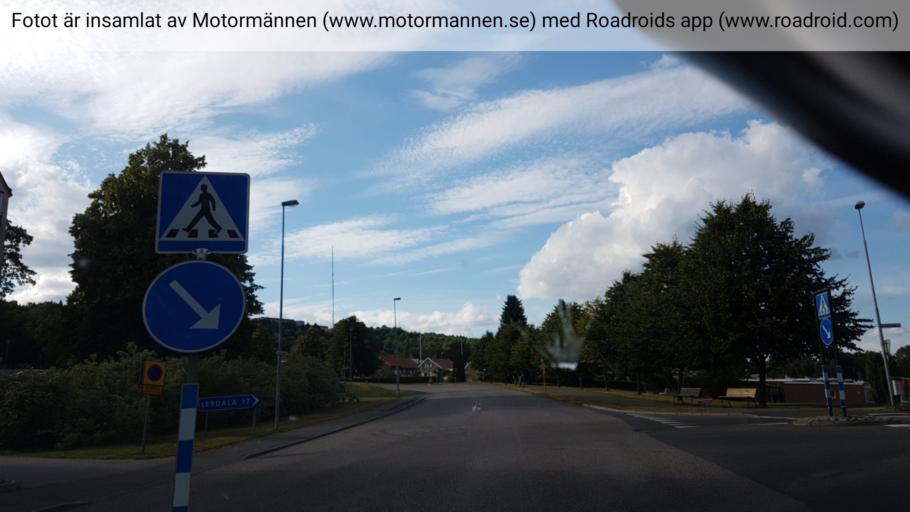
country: SE
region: Vaestra Goetaland
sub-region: Skovde Kommun
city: Skoevde
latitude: 58.3967
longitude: 13.8321
